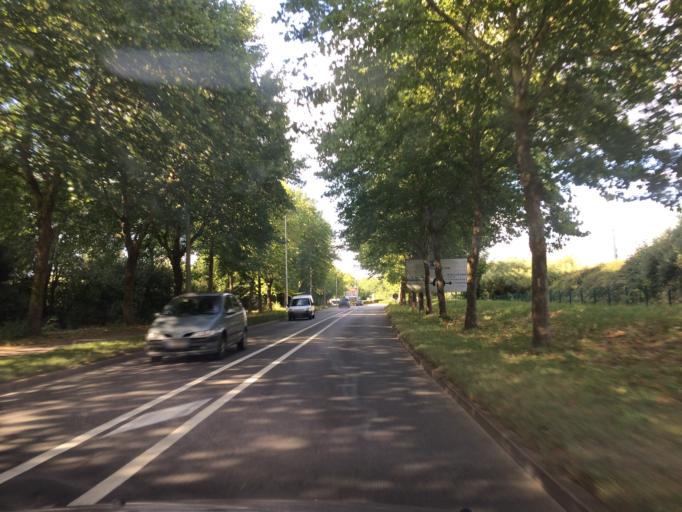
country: FR
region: Ile-de-France
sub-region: Departement de l'Essonne
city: Bondoufle
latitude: 48.6164
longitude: 2.3911
